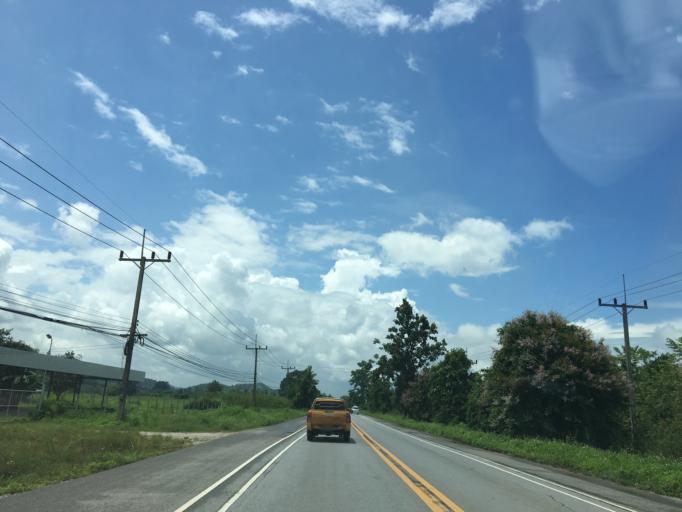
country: TH
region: Chiang Rai
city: Wiang Chai
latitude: 19.7325
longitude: 99.9166
